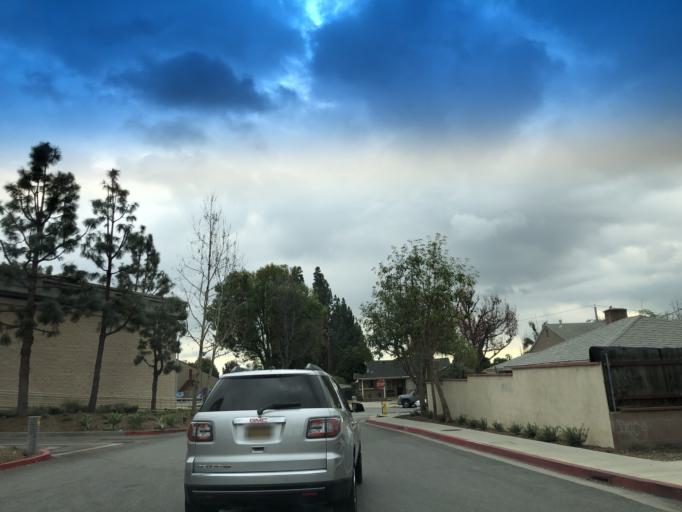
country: US
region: California
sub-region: Los Angeles County
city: East La Mirada
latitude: 33.9414
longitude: -117.9948
